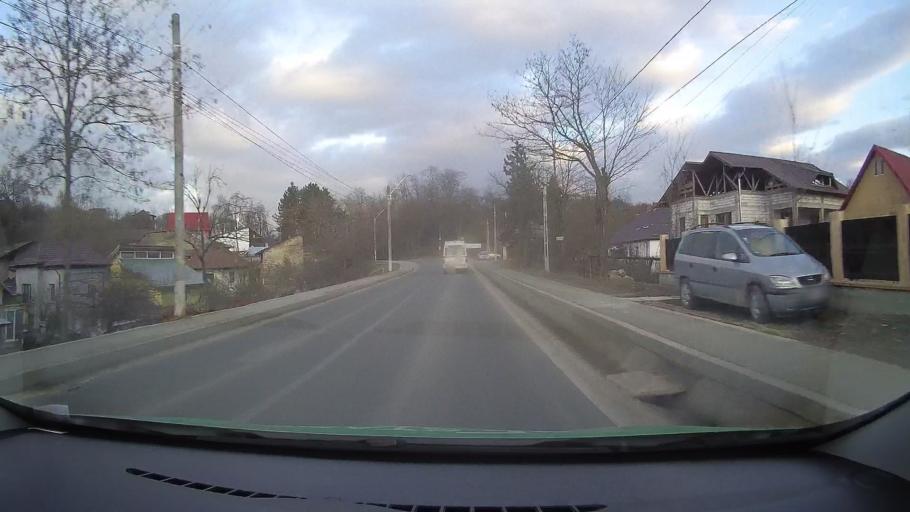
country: RO
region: Dambovita
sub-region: Municipiul Moreni
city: Moreni
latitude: 44.9799
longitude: 25.6270
